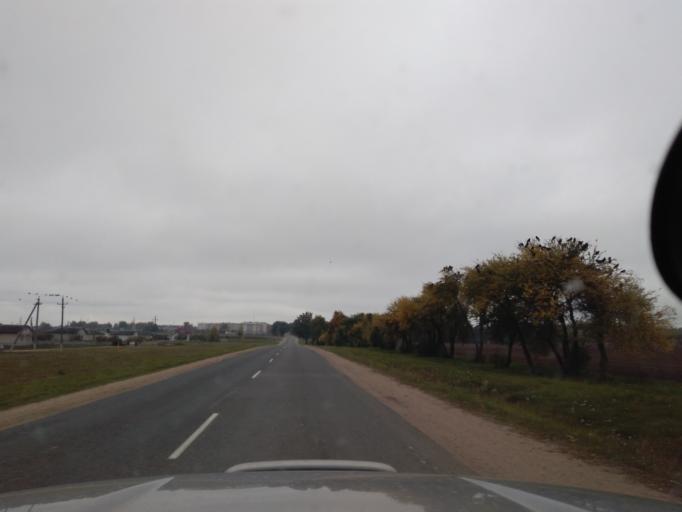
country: BY
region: Minsk
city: Kapyl'
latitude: 53.1499
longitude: 27.1302
